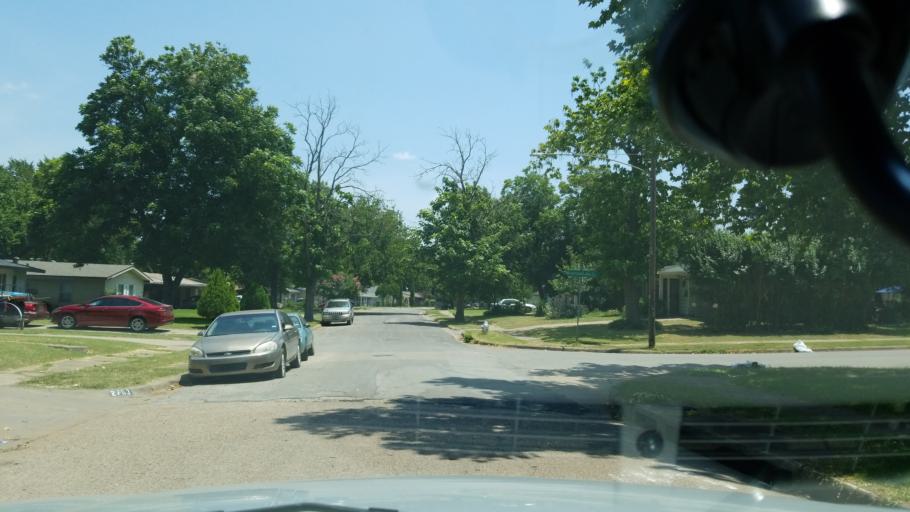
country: US
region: Texas
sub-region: Dallas County
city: Cockrell Hill
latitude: 32.7218
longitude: -96.8642
